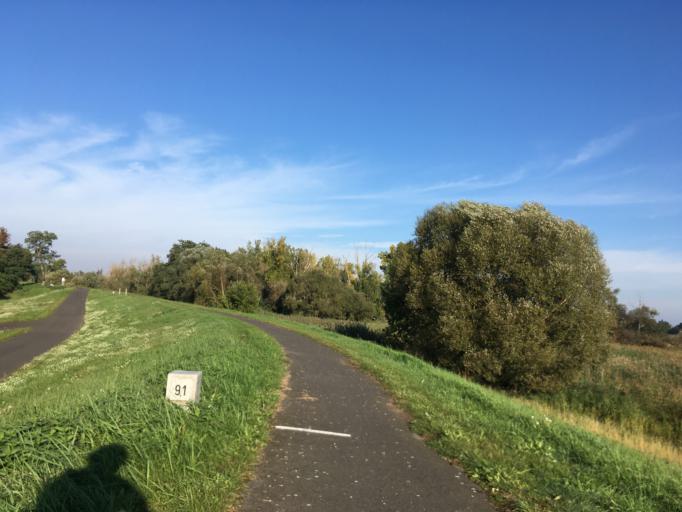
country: PL
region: Lubusz
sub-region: Powiat slubicki
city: Gorzyca
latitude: 52.4973
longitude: 14.6298
